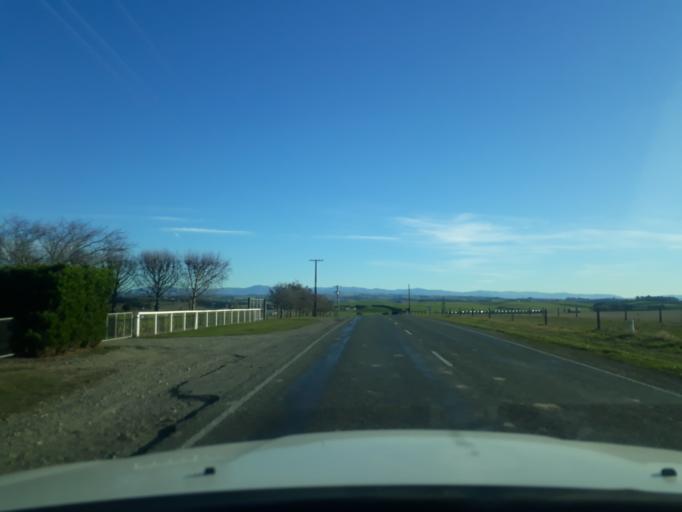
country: NZ
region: Canterbury
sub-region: Timaru District
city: Timaru
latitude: -44.3364
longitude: 171.2196
